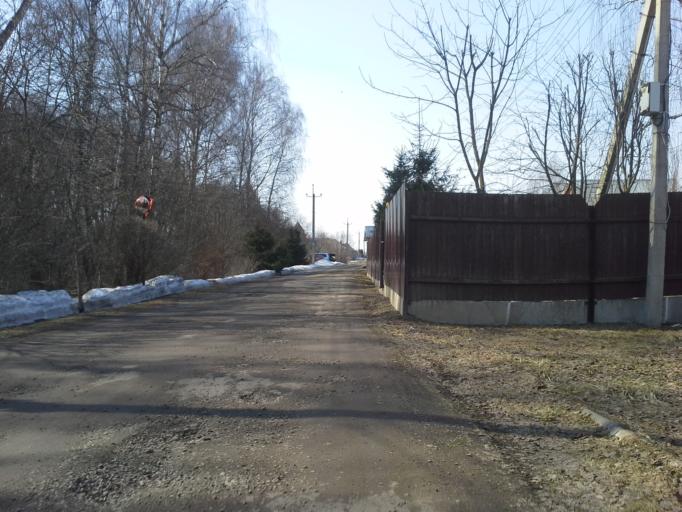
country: RU
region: Moskovskaya
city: Filimonki
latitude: 55.5443
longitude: 37.3843
